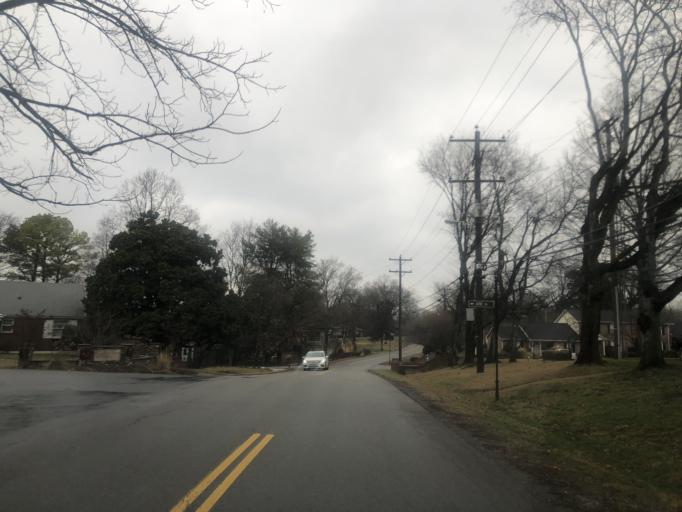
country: US
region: Tennessee
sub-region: Davidson County
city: Nashville
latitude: 36.1690
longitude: -86.6924
